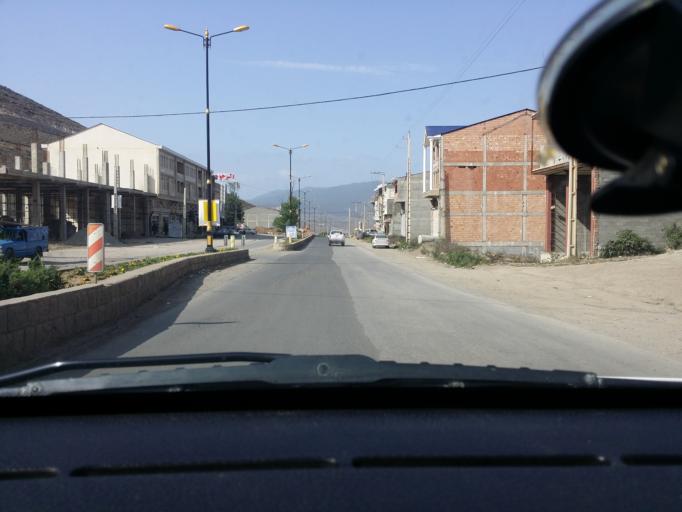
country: IR
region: Mazandaran
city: `Abbasabad
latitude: 36.5101
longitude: 51.1587
